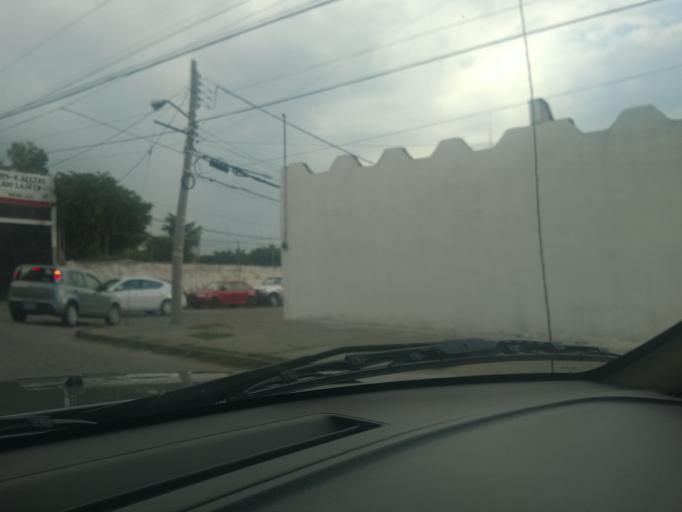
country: MX
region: Guanajuato
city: Leon
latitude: 21.1199
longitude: -101.6538
